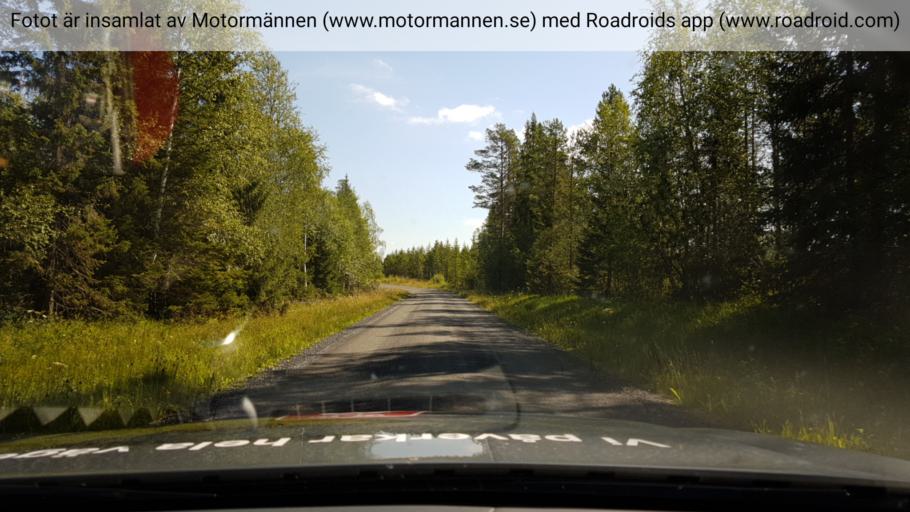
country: SE
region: Jaemtland
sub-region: OEstersunds Kommun
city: Lit
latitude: 63.3490
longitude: 15.3528
